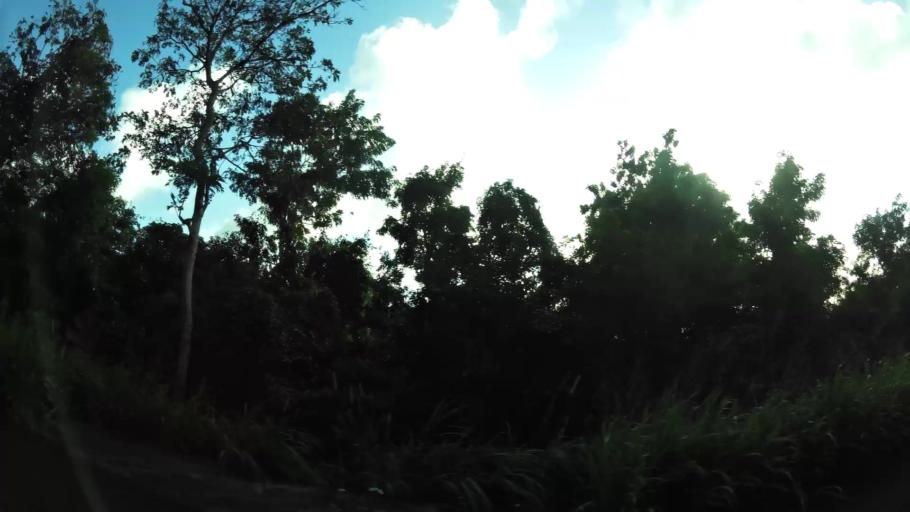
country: GP
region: Guadeloupe
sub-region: Guadeloupe
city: Pointe-Noire
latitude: 16.1830
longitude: -61.7682
